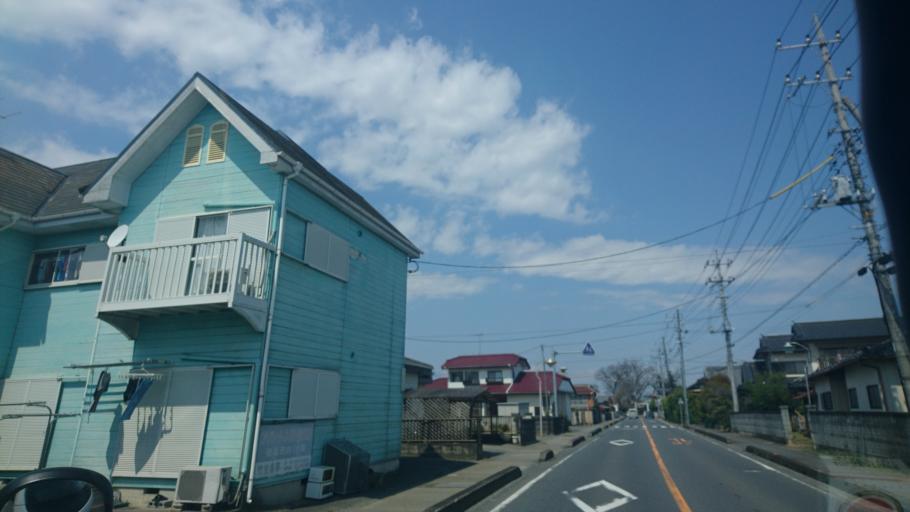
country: JP
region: Ibaraki
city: Yuki
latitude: 36.2844
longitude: 139.8966
